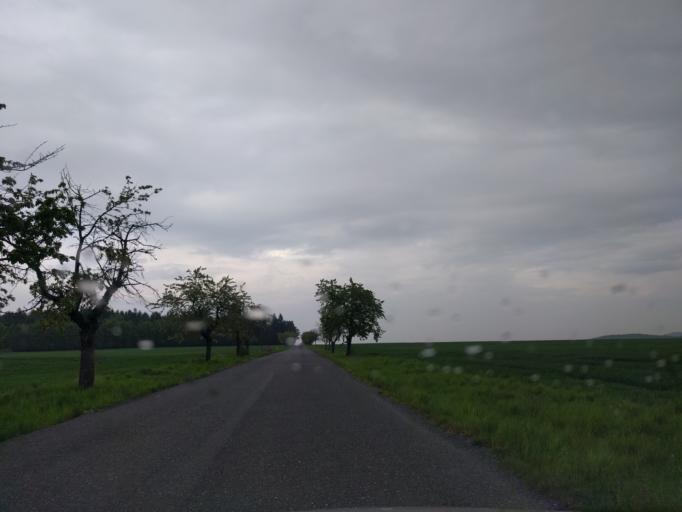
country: CZ
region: Central Bohemia
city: Dobris
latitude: 49.7267
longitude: 14.1482
